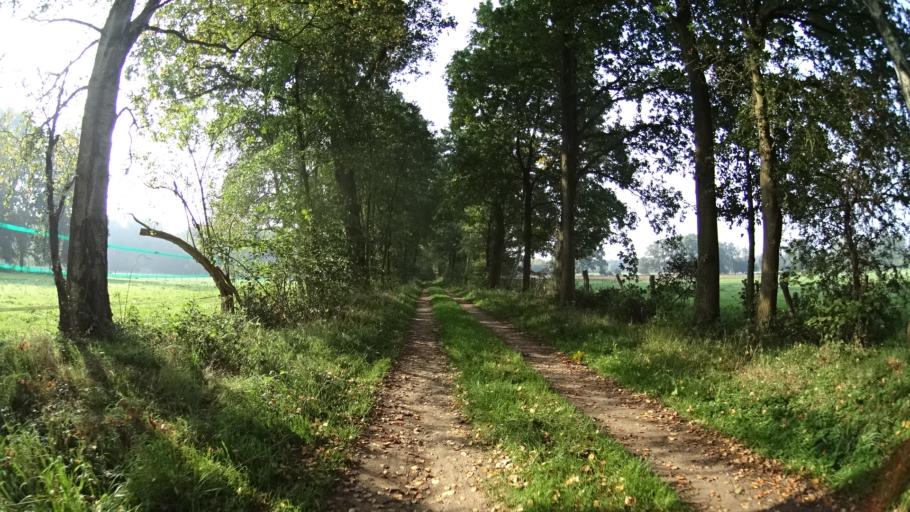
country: DE
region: Lower Saxony
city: Reppenstedt
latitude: 53.2249
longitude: 10.3425
